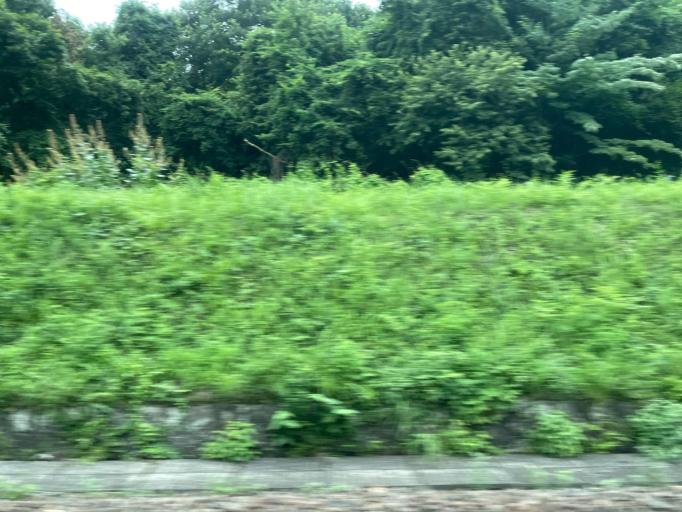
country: JP
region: Tochigi
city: Kuroiso
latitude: 37.0066
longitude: 140.0923
